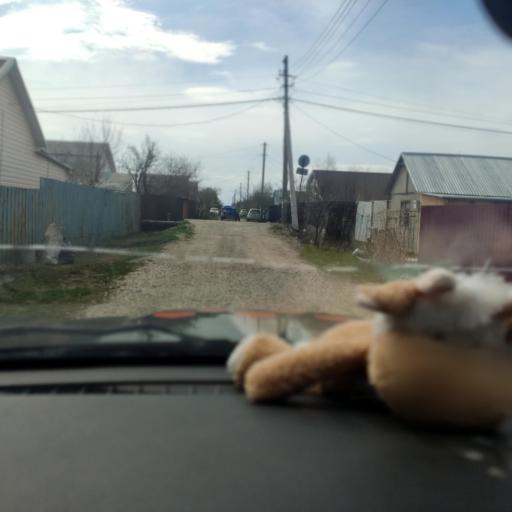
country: RU
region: Samara
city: Podstepki
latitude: 53.5953
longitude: 49.2255
